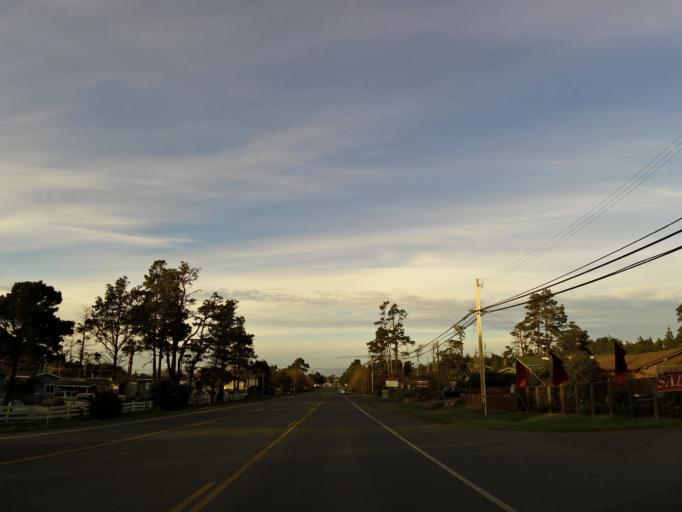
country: US
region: California
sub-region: Mendocino County
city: Fort Bragg
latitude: 39.4038
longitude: -123.8089
